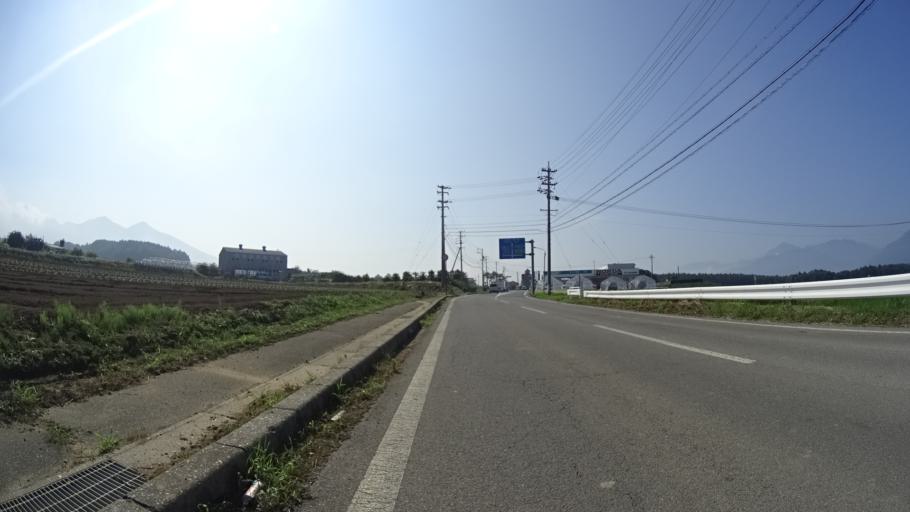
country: JP
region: Nagano
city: Chino
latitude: 35.9479
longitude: 138.2413
